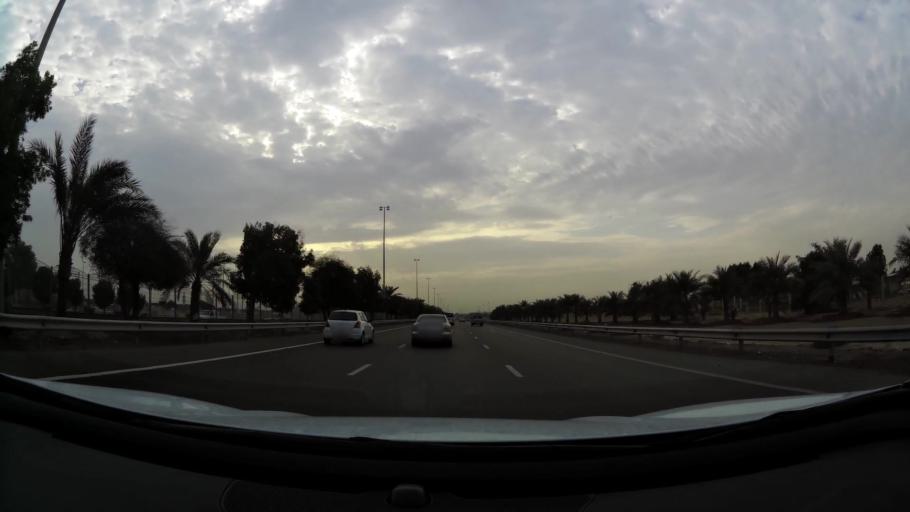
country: AE
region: Abu Dhabi
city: Abu Dhabi
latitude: 24.2890
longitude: 54.6373
